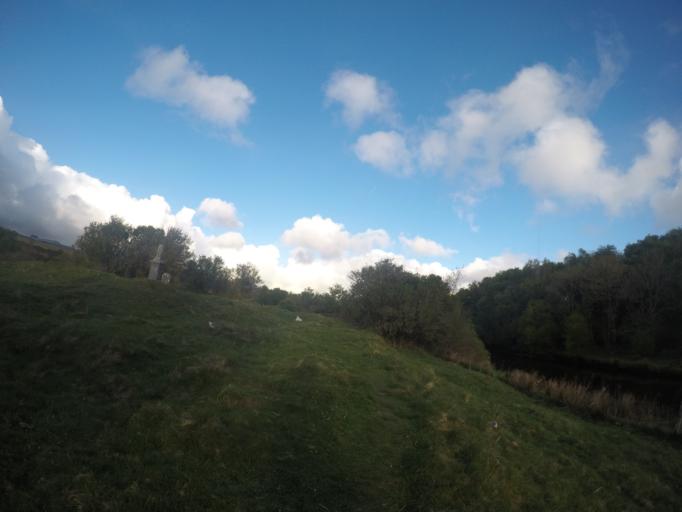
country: GB
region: Scotland
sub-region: Highland
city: Isle of Skye
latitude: 57.4531
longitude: -6.3059
